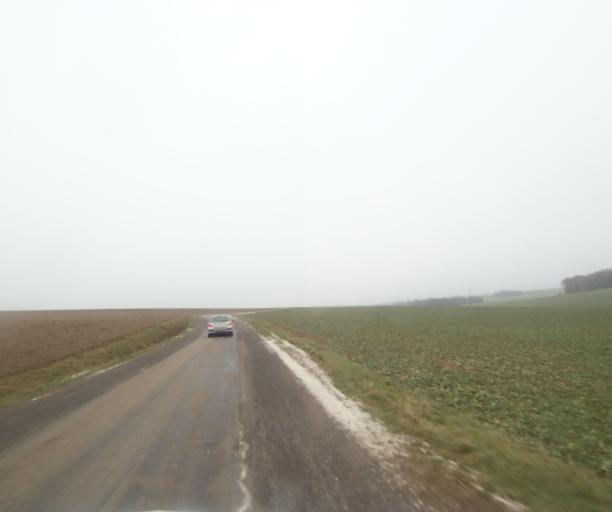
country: FR
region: Champagne-Ardenne
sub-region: Departement de la Haute-Marne
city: Bienville
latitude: 48.5336
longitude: 5.0545
